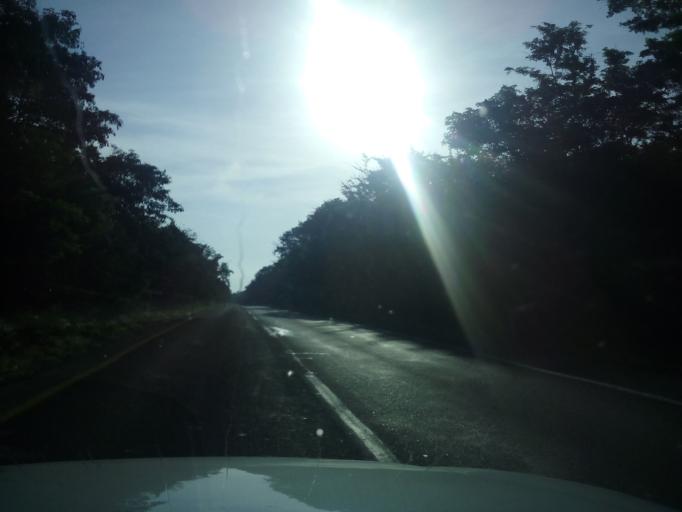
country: MX
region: Yucatan
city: Tinum
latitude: 20.7090
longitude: -88.4657
